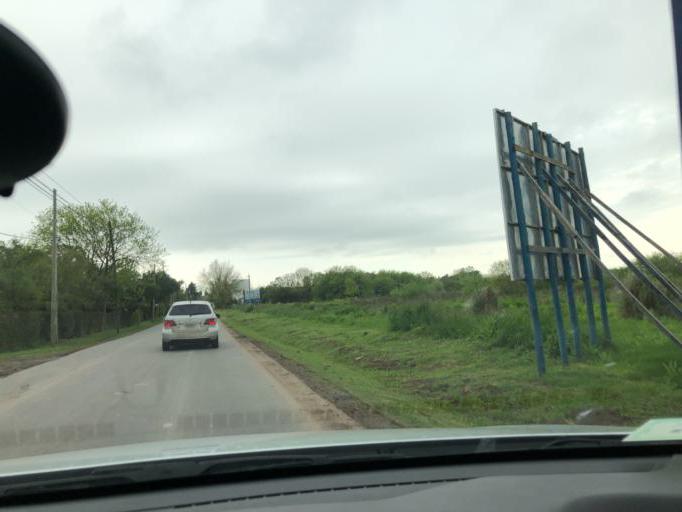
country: AR
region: Buenos Aires
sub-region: Partido de La Plata
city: La Plata
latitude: -34.8984
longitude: -58.0678
